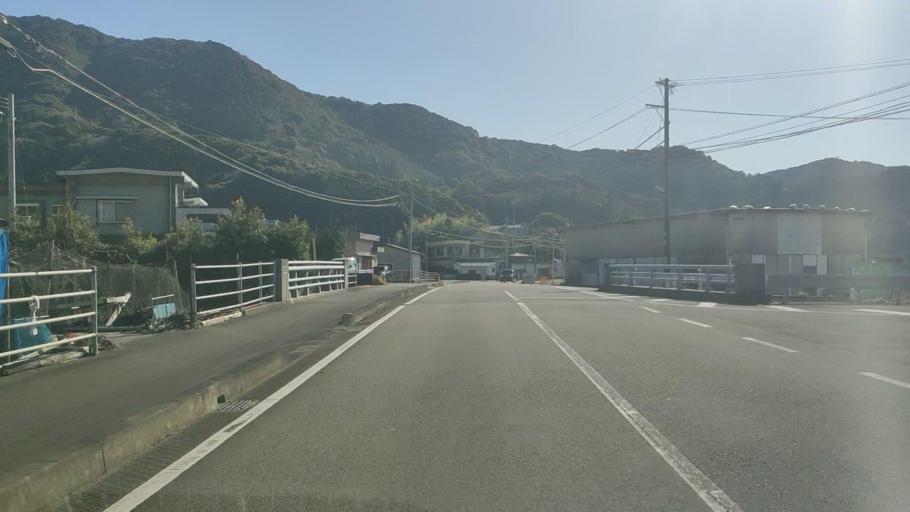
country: JP
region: Oita
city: Saiki
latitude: 32.8030
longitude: 131.8991
